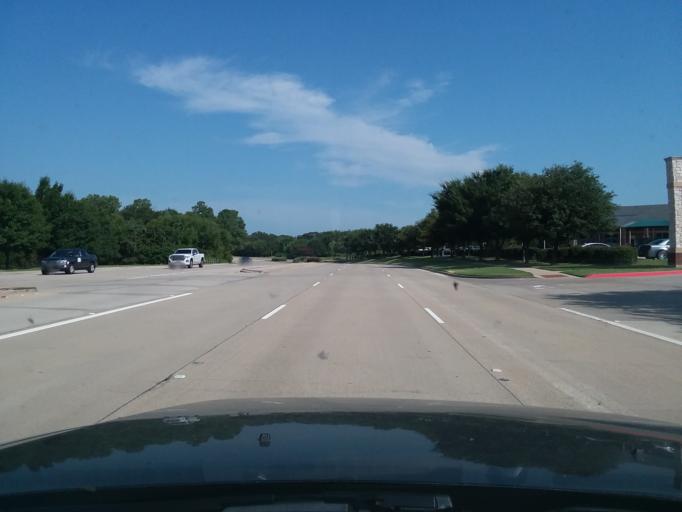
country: US
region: Texas
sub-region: Denton County
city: Flower Mound
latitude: 33.0119
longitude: -97.0464
